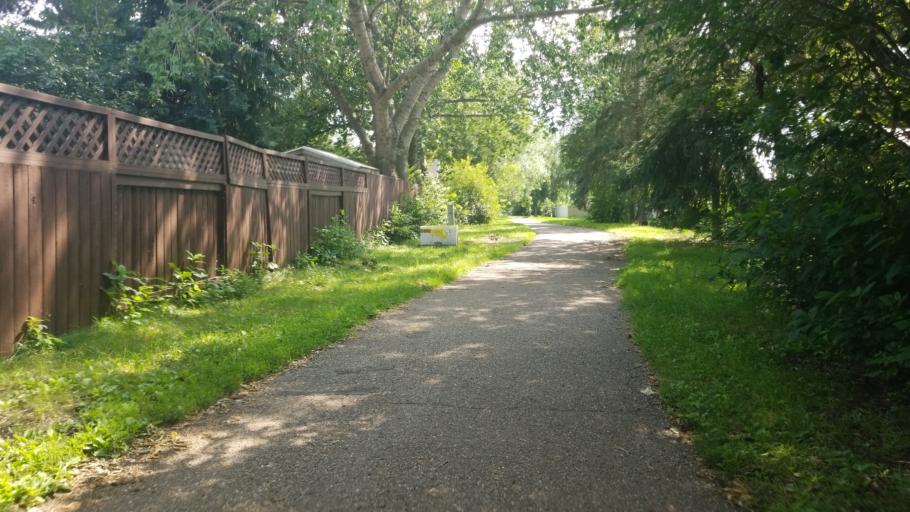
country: CA
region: Saskatchewan
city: Lloydminster
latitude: 53.2691
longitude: -110.0176
